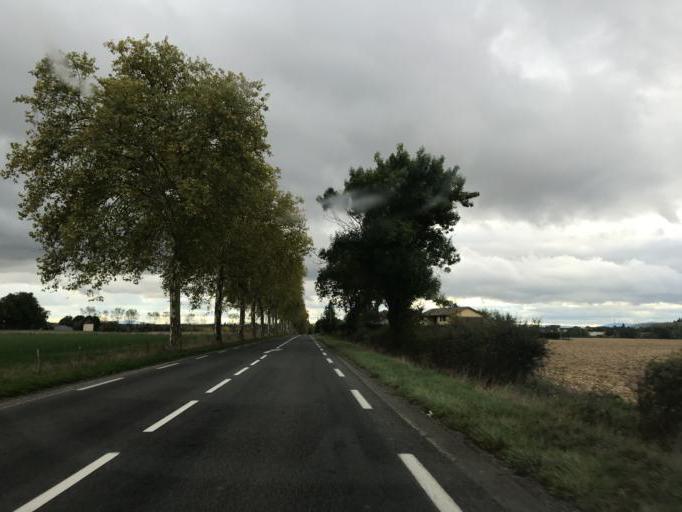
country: FR
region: Rhone-Alpes
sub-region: Departement de l'Ain
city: Saint-Trivier-sur-Moignans
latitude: 46.0831
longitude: 4.9101
